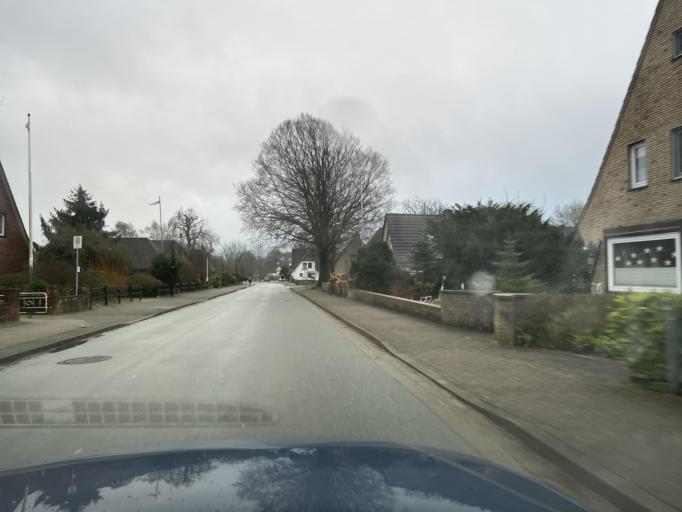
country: DE
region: Schleswig-Holstein
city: Wesseln
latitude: 54.2076
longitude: 9.0759
